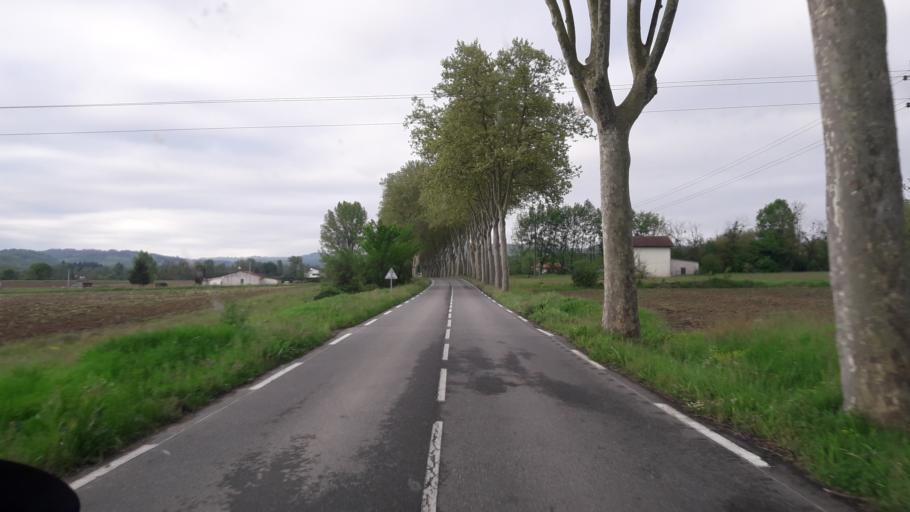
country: FR
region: Midi-Pyrenees
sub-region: Departement de la Haute-Garonne
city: Cazeres
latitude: 43.1962
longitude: 1.1039
